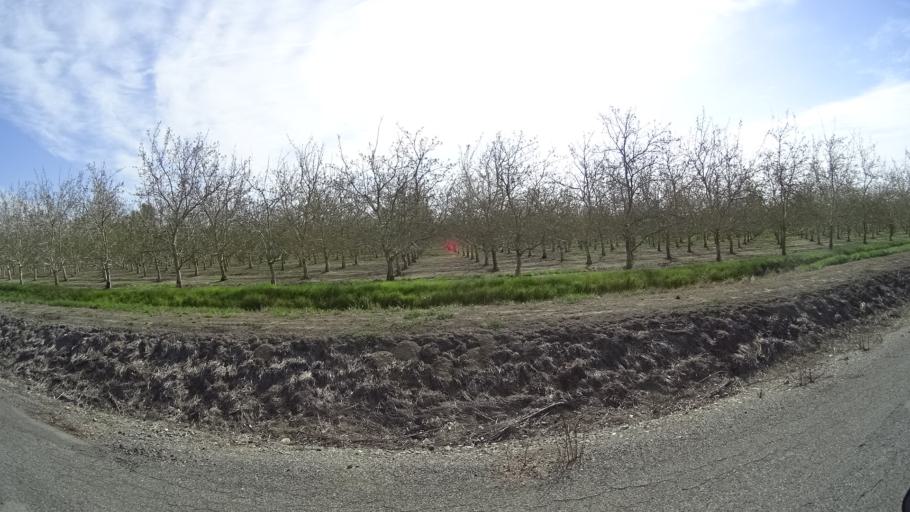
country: US
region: California
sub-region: Glenn County
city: Hamilton City
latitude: 39.6215
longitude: -122.0463
